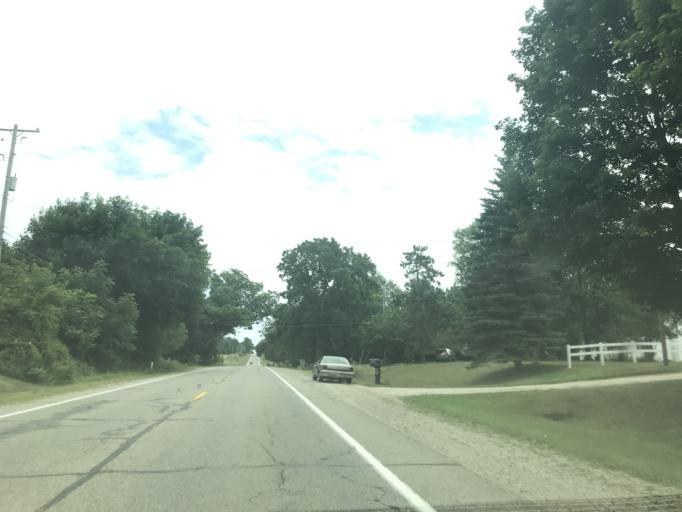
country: US
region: Michigan
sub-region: Clinton County
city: Wacousta
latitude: 42.7923
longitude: -84.7097
